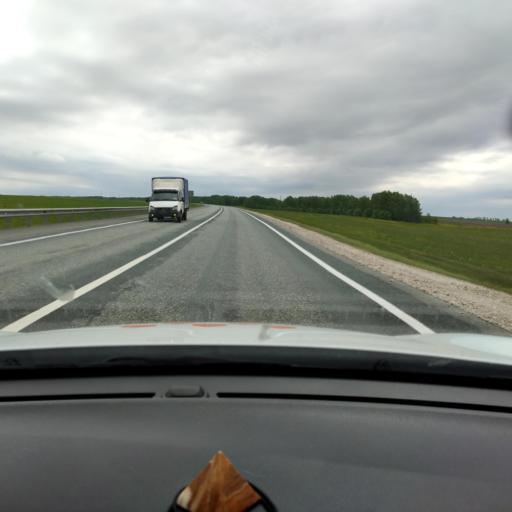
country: RU
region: Tatarstan
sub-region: Alekseyevskiy Rayon
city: Alekseyevskoye
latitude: 55.3956
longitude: 49.8722
